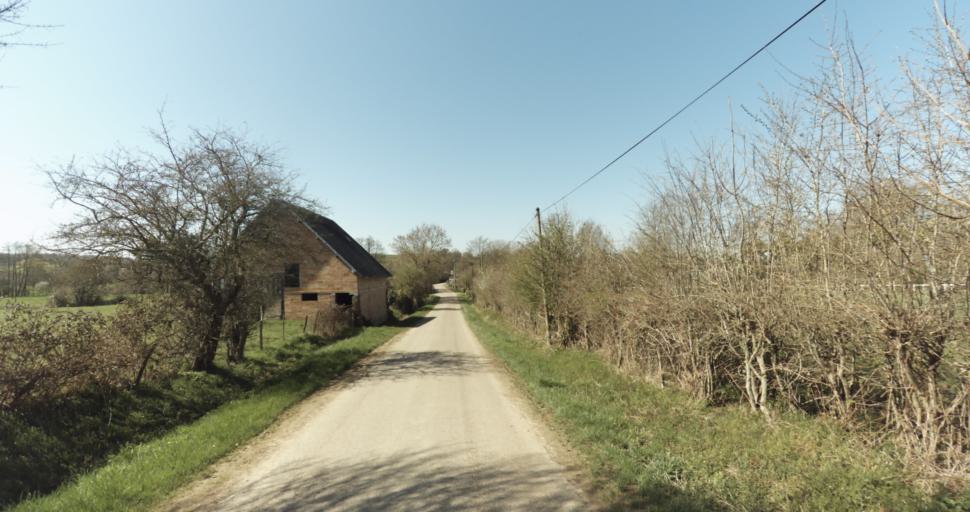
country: FR
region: Lower Normandy
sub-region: Departement du Calvados
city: Saint-Pierre-sur-Dives
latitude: 48.9889
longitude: 0.0333
